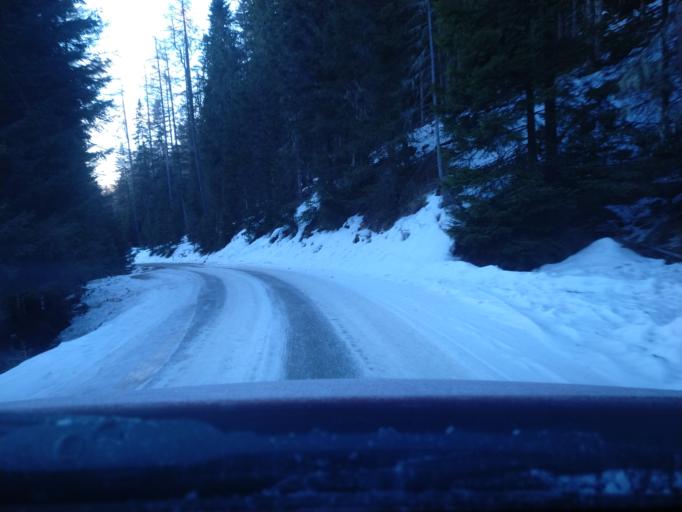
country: AT
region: Carinthia
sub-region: Politischer Bezirk Villach Land
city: Arriach
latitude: 46.7032
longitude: 13.8999
